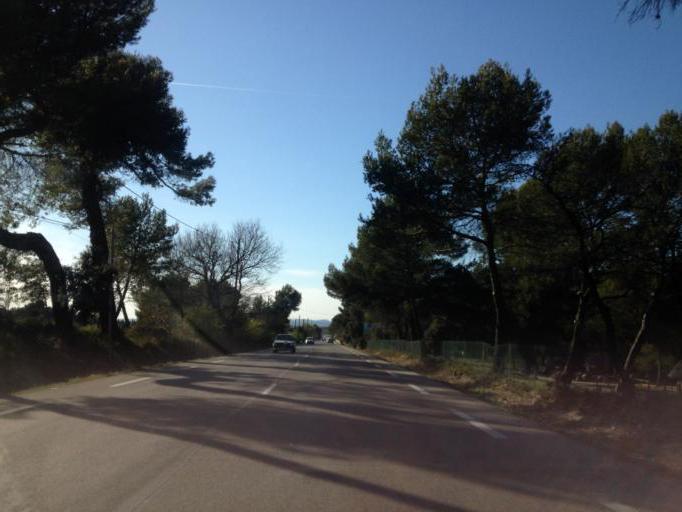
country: FR
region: Provence-Alpes-Cote d'Azur
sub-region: Departement des Bouches-du-Rhone
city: Saint-Cannat
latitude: 43.6068
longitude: 5.3348
